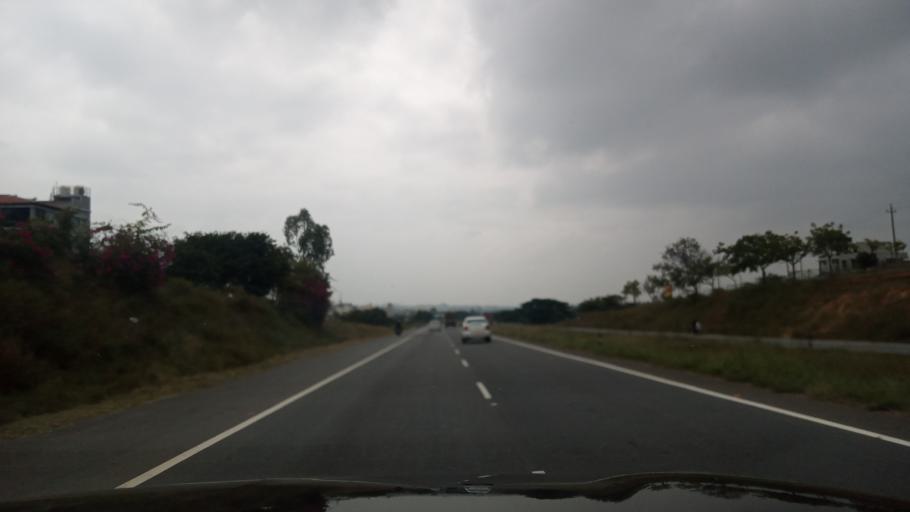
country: IN
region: Karnataka
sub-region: Bangalore Urban
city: Bangalore
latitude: 12.9610
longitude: 77.4715
